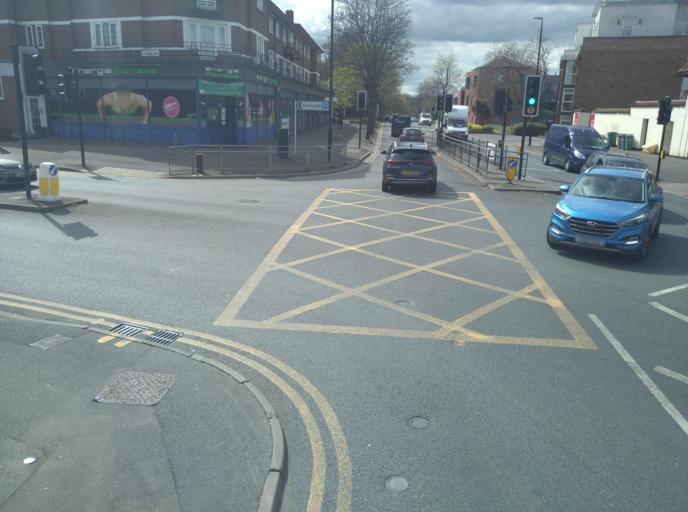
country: GB
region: England
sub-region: Greater London
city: Carshalton
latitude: 51.3573
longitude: -0.1491
